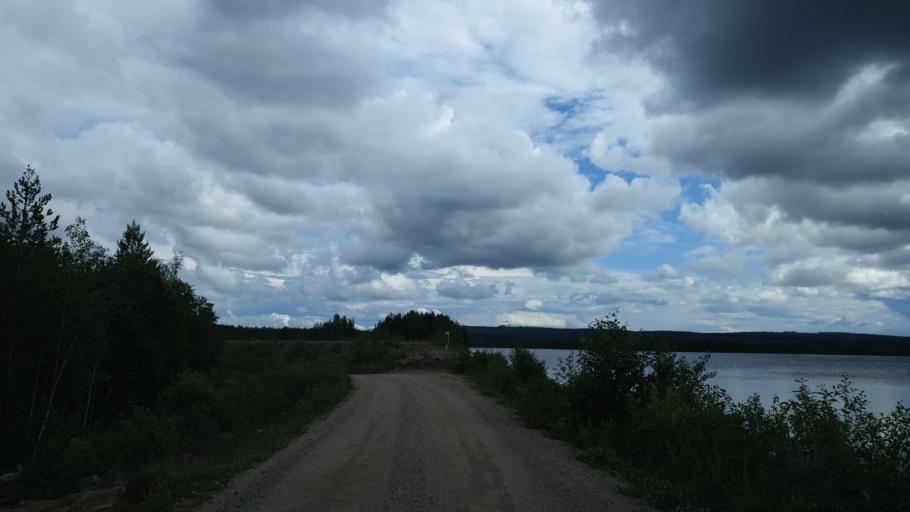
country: SE
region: Jaemtland
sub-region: Harjedalens Kommun
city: Sveg
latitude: 62.0421
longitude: 14.4838
